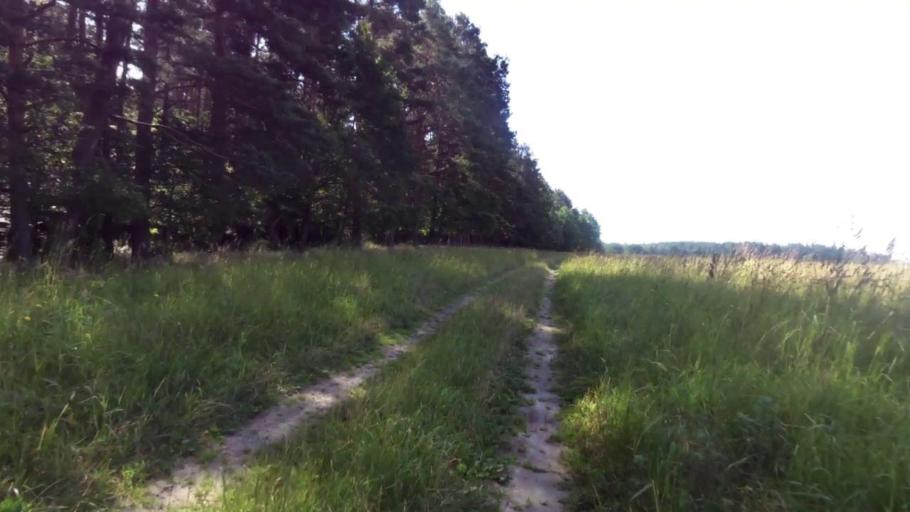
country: PL
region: West Pomeranian Voivodeship
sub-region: Powiat swidwinski
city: Polczyn-Zdroj
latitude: 53.8886
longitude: 16.0916
